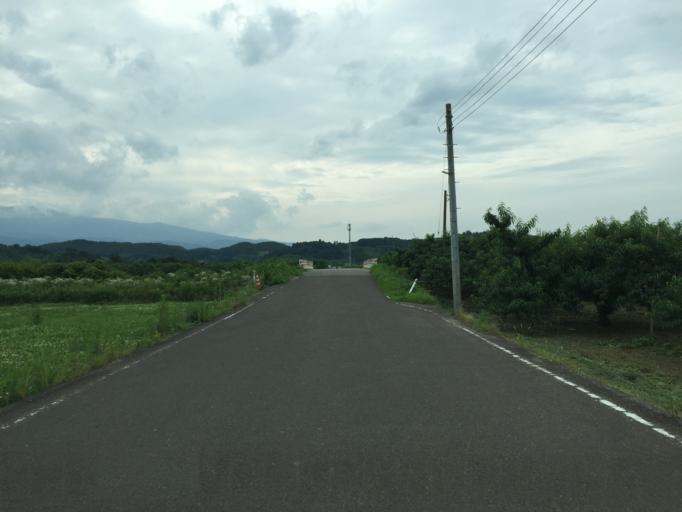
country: JP
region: Fukushima
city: Fukushima-shi
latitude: 37.7156
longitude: 140.4446
